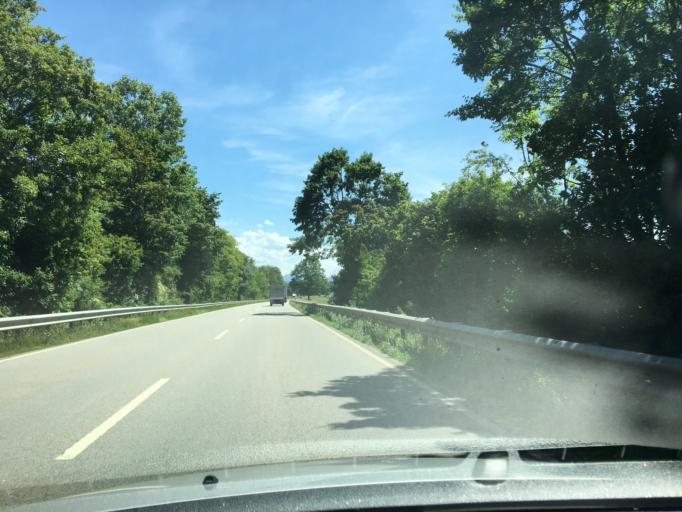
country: DE
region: Bavaria
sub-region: Upper Bavaria
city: Laufen
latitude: 47.8953
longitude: 12.9564
